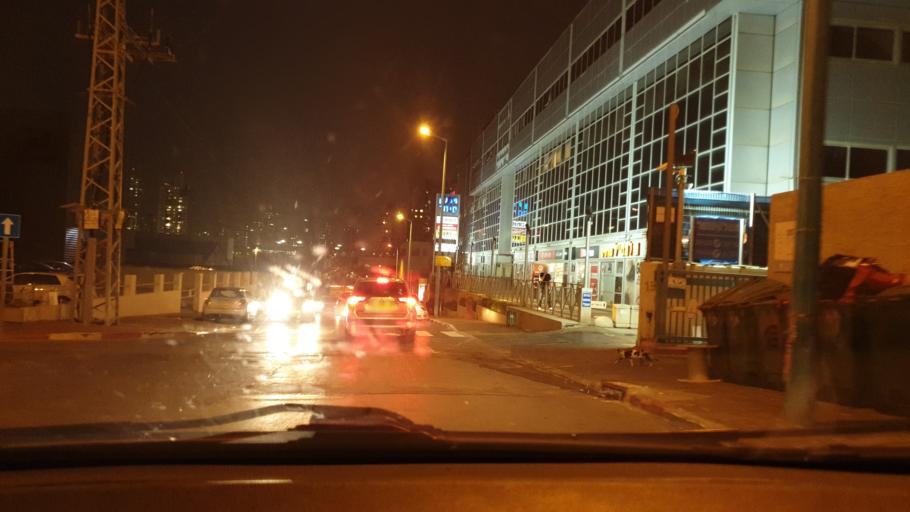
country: IL
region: Tel Aviv
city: Giv`at Shemu'el
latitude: 32.0878
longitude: 34.8535
